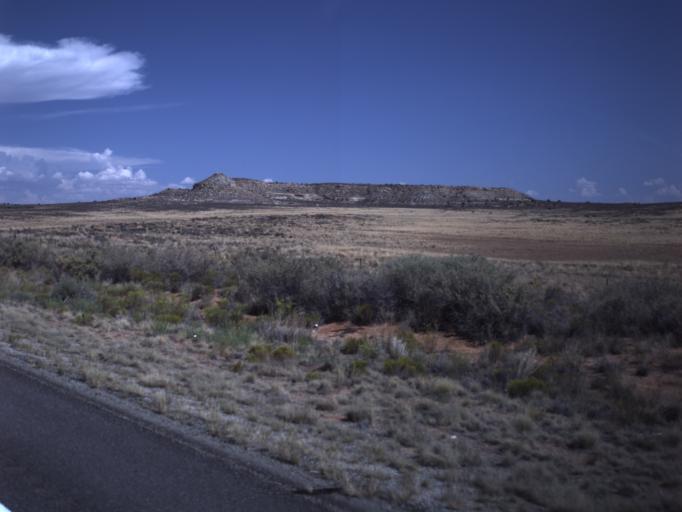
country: US
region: Utah
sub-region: San Juan County
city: Blanding
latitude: 37.3378
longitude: -109.5199
